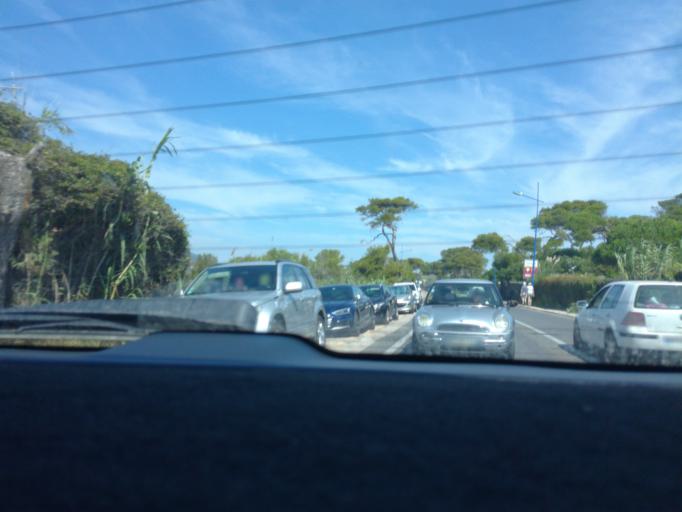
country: FR
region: Provence-Alpes-Cote d'Azur
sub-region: Departement du Var
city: Hyeres
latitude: 43.0550
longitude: 6.1471
